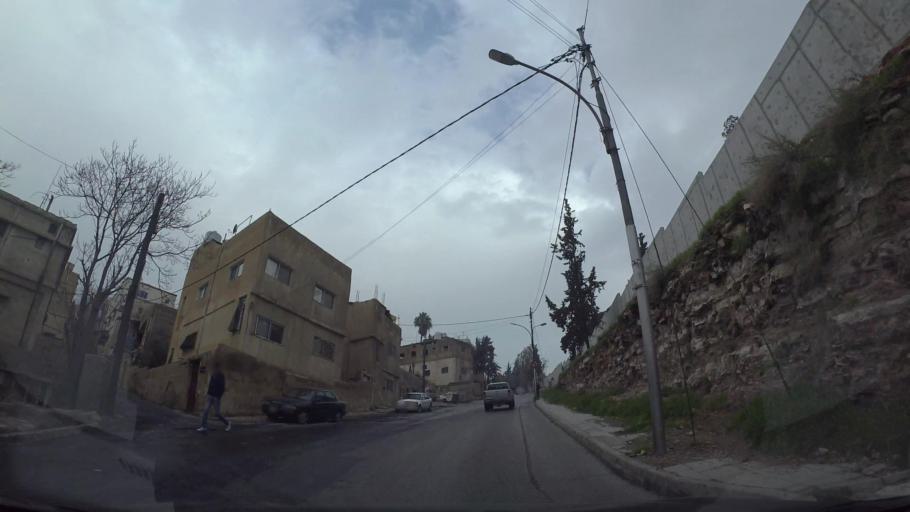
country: JO
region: Amman
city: Amman
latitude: 31.9563
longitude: 35.9444
